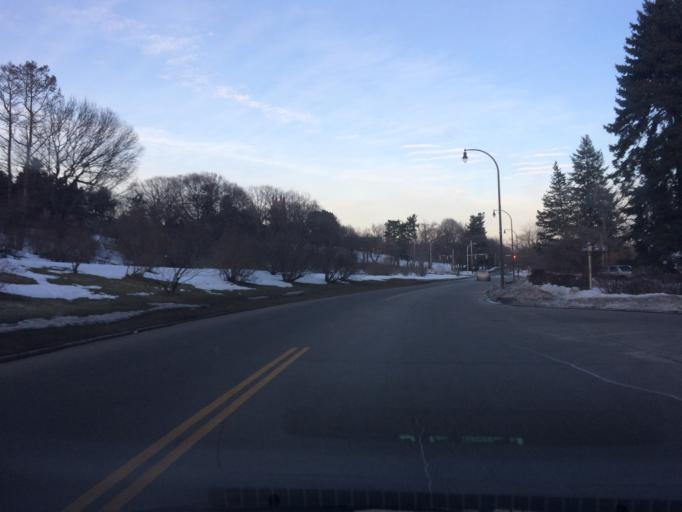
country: US
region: New York
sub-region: Monroe County
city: Rochester
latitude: 43.1297
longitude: -77.6035
